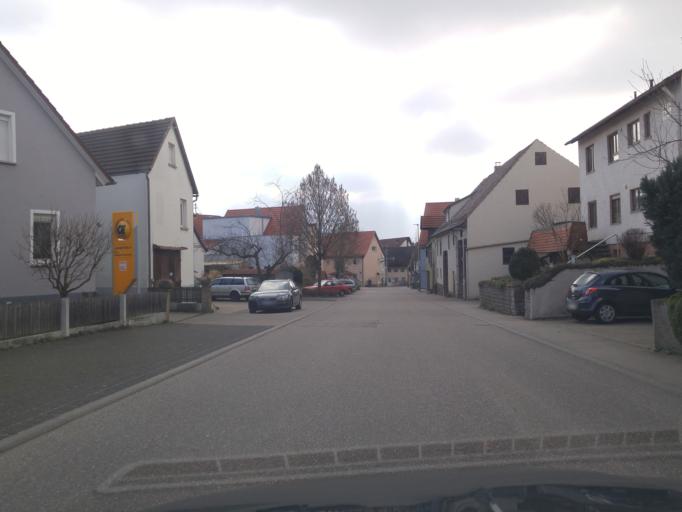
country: DE
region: Baden-Wuerttemberg
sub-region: Regierungsbezirk Stuttgart
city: Ilsfeld
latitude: 49.0574
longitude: 9.2498
